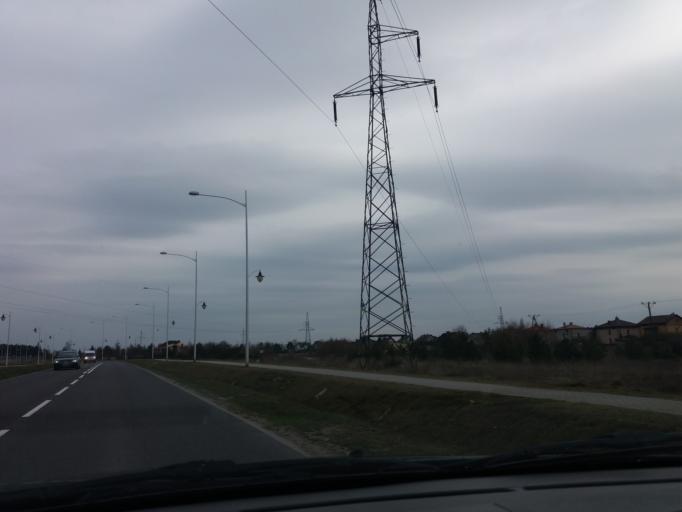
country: PL
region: Masovian Voivodeship
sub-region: Powiat mlawski
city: Mlawa
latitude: 53.1292
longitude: 20.3695
